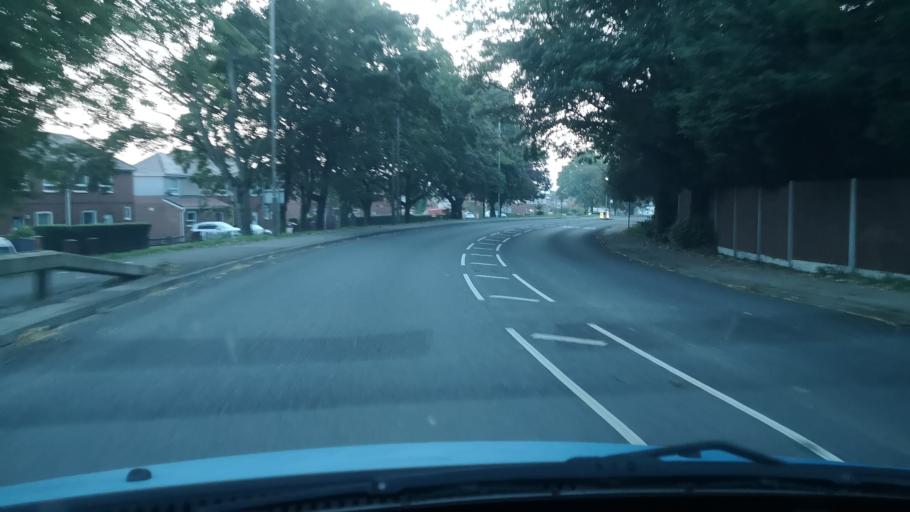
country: GB
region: England
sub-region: City and Borough of Wakefield
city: Low Ackworth
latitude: 53.6409
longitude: -1.3334
